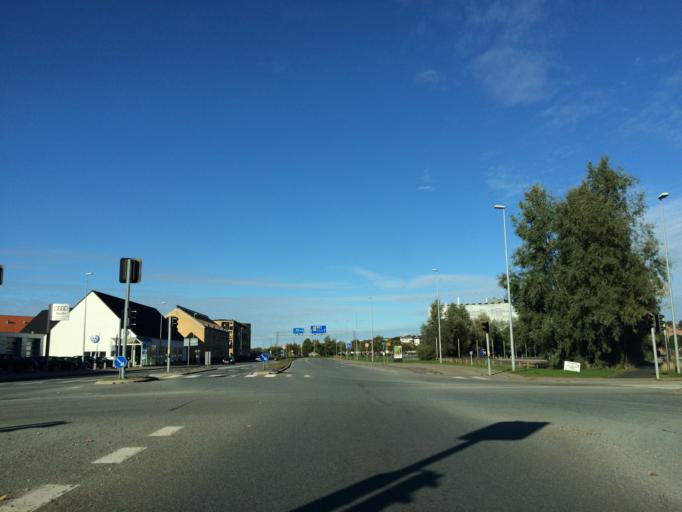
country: DK
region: Central Jutland
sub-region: Randers Kommune
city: Randers
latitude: 56.4540
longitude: 10.0457
